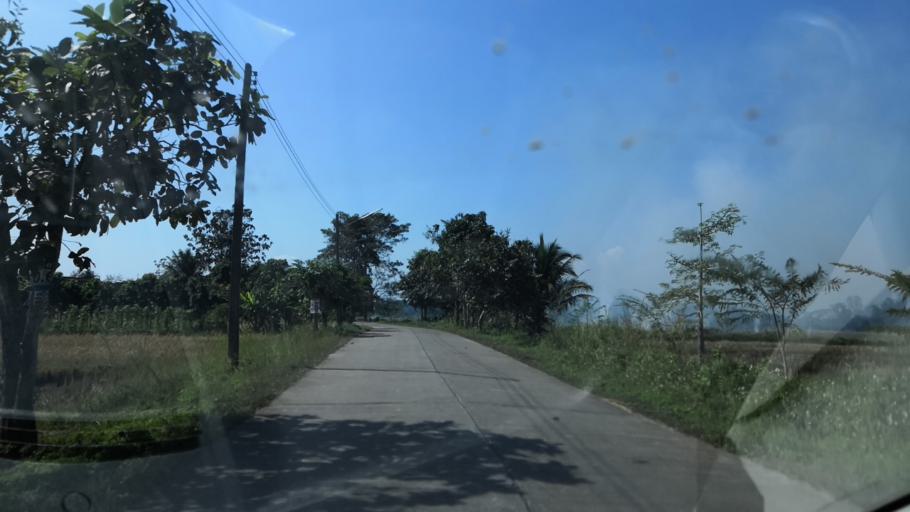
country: TH
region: Chiang Rai
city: Wiang Chai
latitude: 19.8853
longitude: 99.9456
